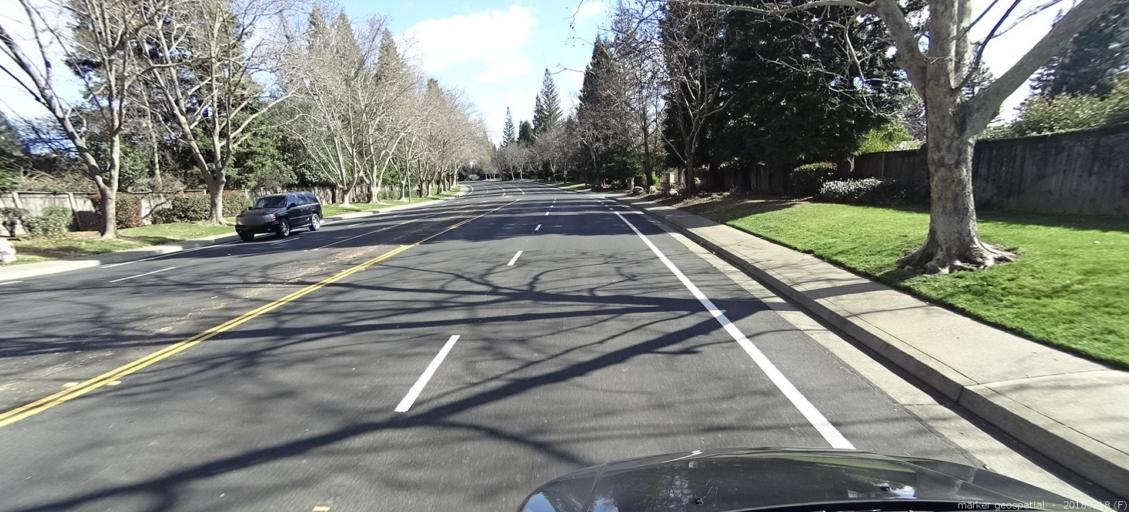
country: US
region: California
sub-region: Sacramento County
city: Folsom
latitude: 38.6844
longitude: -121.1902
